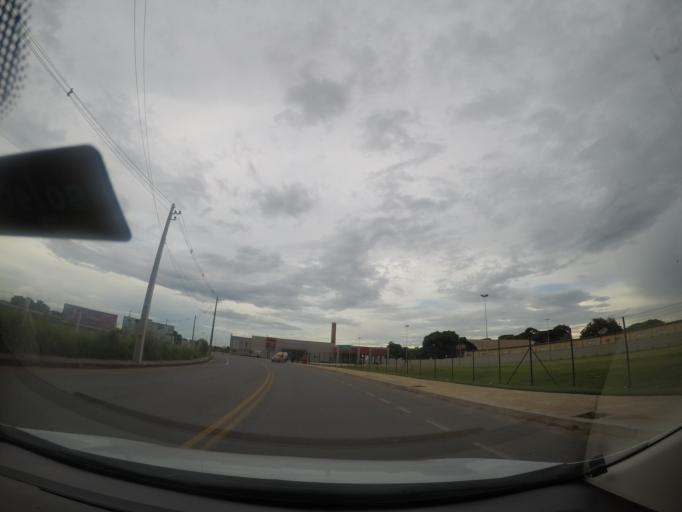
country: BR
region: Goias
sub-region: Goiania
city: Goiania
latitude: -16.6574
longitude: -49.2697
